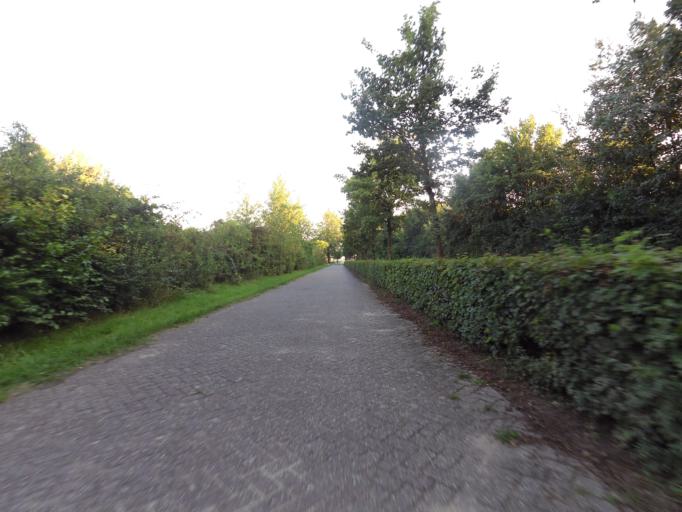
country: NL
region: Gelderland
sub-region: Gemeente Zevenaar
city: Zevenaar
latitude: 51.8644
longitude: 6.0781
